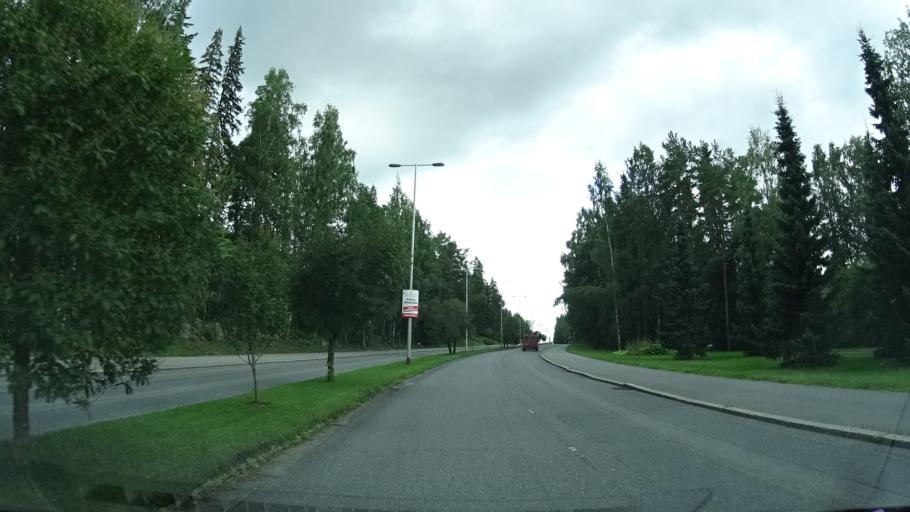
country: FI
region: Pirkanmaa
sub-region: Etelae-Pirkanmaa
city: Valkeakoski
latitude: 61.2589
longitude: 24.0347
